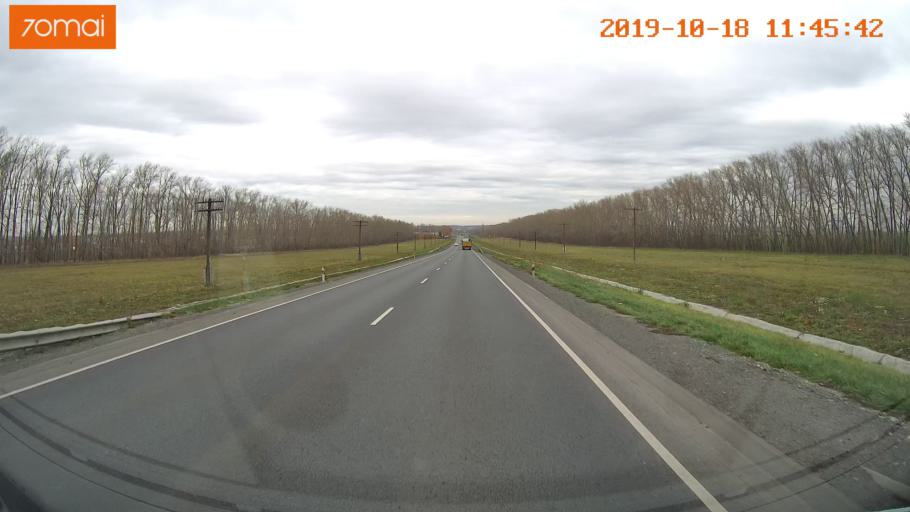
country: RU
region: Rjazan
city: Mikhaylov
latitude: 54.2127
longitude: 38.9733
